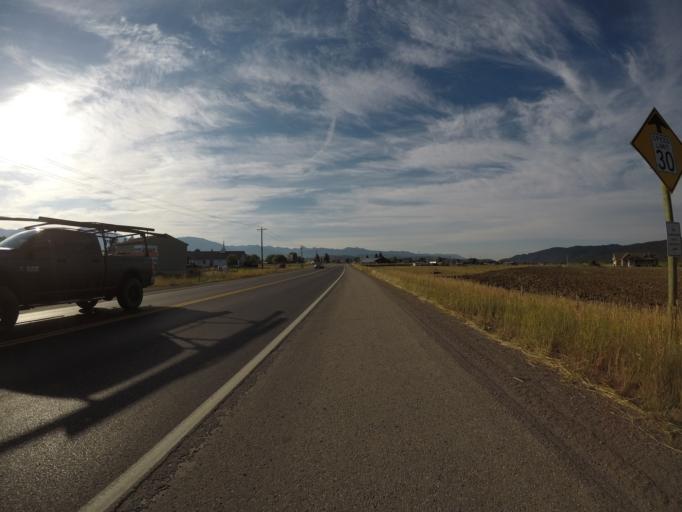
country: US
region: Wyoming
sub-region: Lincoln County
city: Afton
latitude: 42.9269
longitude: -111.0059
